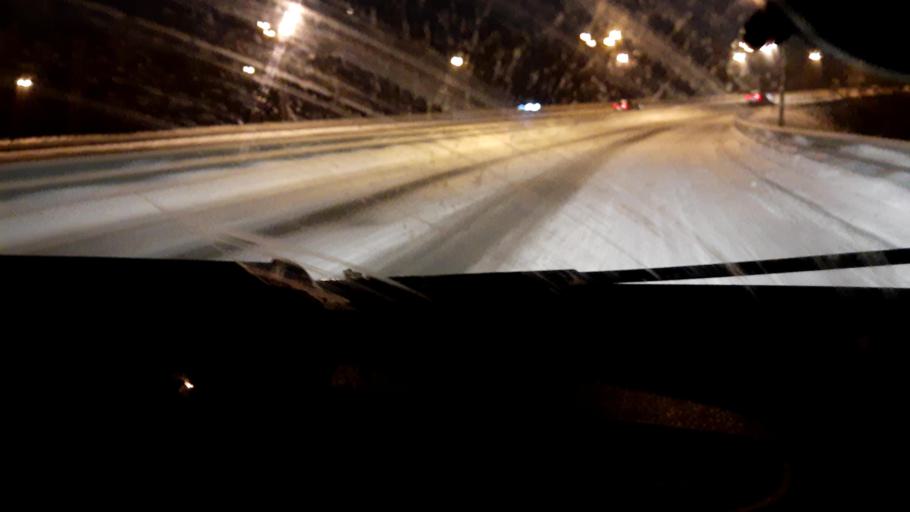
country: RU
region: Bashkortostan
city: Ufa
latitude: 54.6462
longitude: 55.9335
